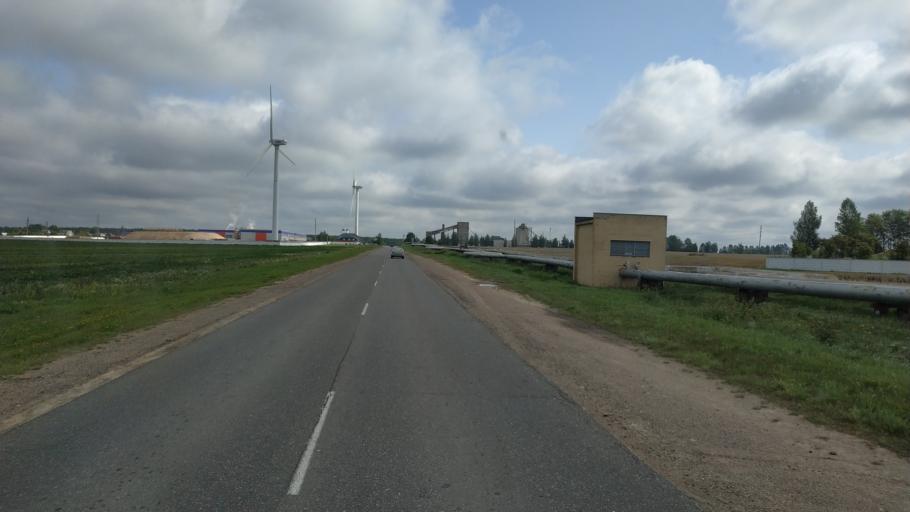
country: BY
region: Mogilev
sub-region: Mahilyowski Rayon
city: Veyno
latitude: 53.8369
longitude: 30.3709
